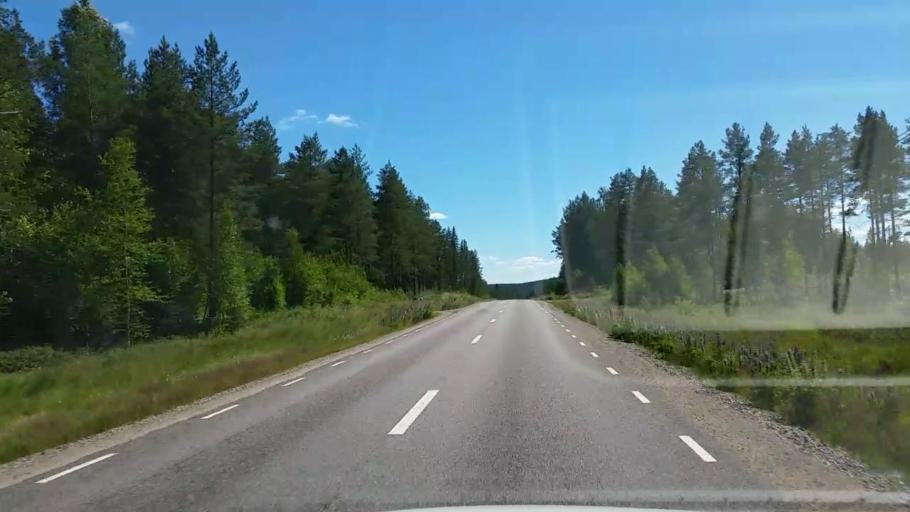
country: SE
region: Gaevleborg
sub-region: Ovanakers Kommun
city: Edsbyn
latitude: 61.4377
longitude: 15.7164
